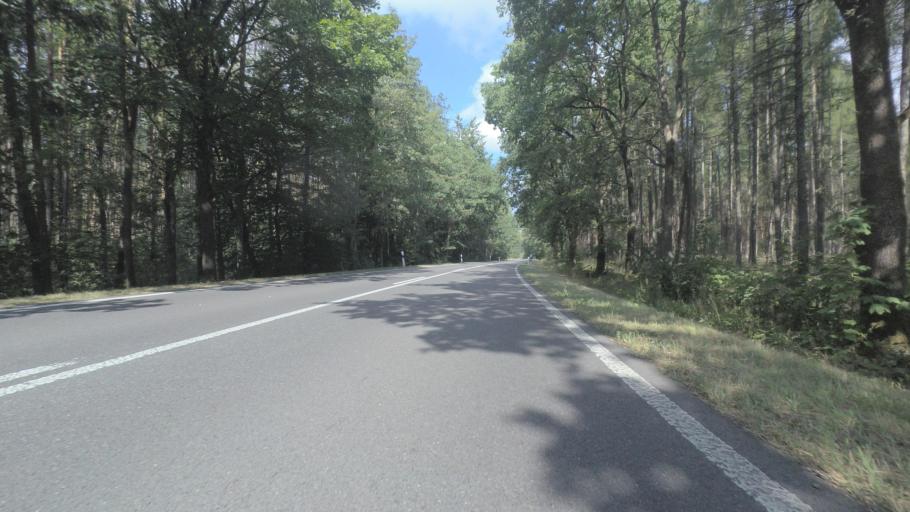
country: DE
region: Brandenburg
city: Walsleben
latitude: 52.9862
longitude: 12.6989
